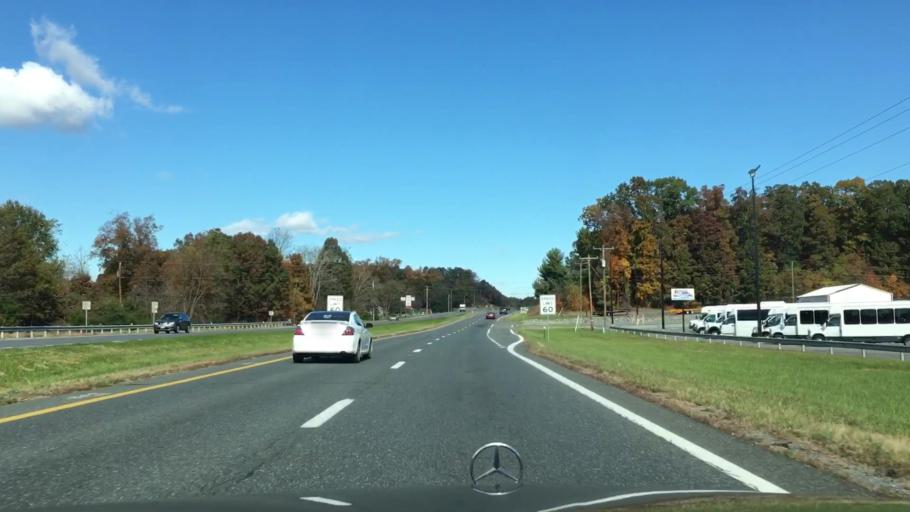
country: US
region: Virginia
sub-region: Campbell County
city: Altavista
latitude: 37.1996
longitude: -79.2033
